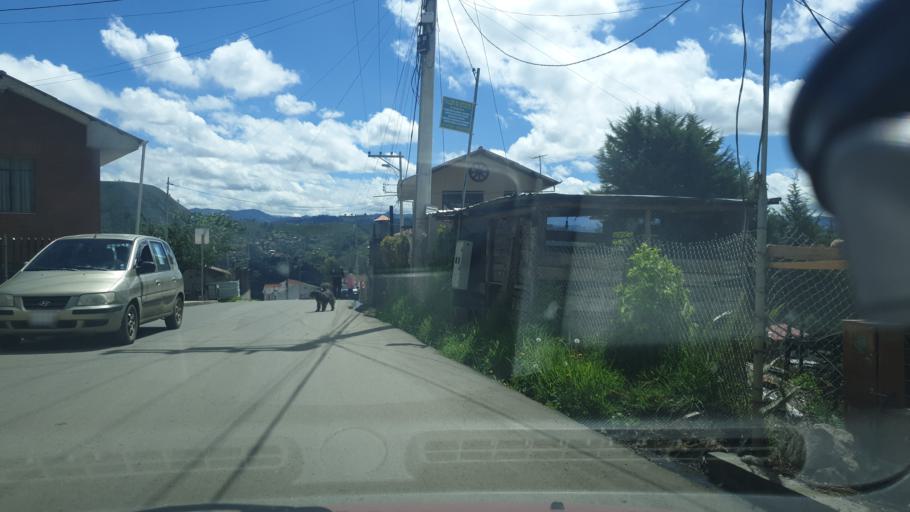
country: EC
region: Azuay
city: Llacao
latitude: -2.8631
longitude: -78.9070
